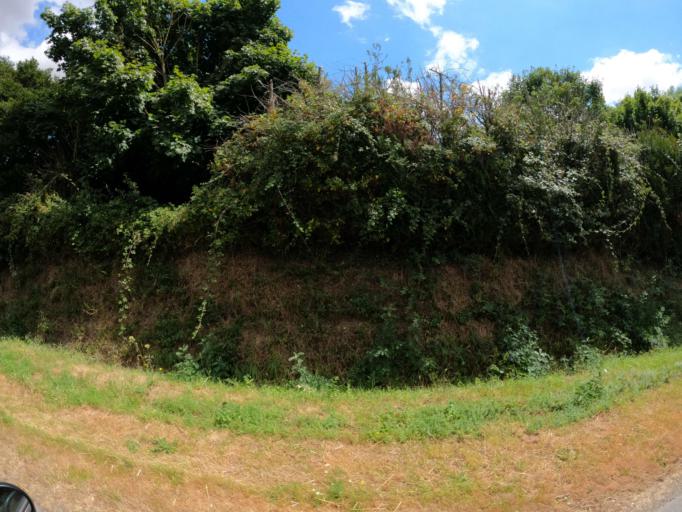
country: FR
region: Pays de la Loire
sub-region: Departement de Maine-et-Loire
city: Mire
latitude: 47.7623
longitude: -0.4858
